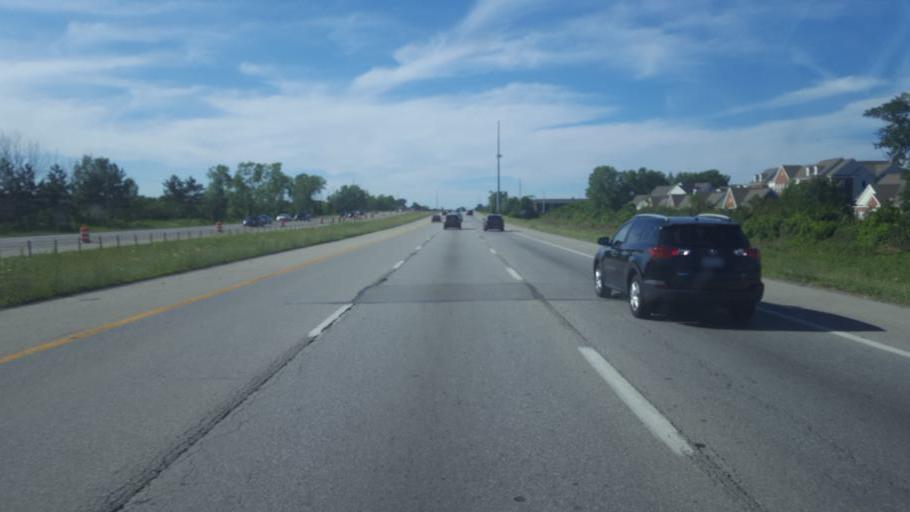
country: US
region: Ohio
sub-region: Franklin County
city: Hilliard
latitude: 40.0589
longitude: -83.1307
